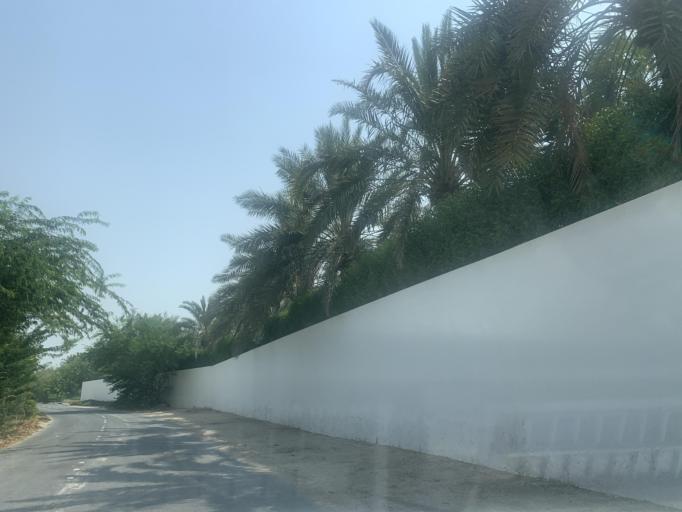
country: BH
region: Central Governorate
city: Madinat Hamad
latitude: 26.1701
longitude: 50.4532
